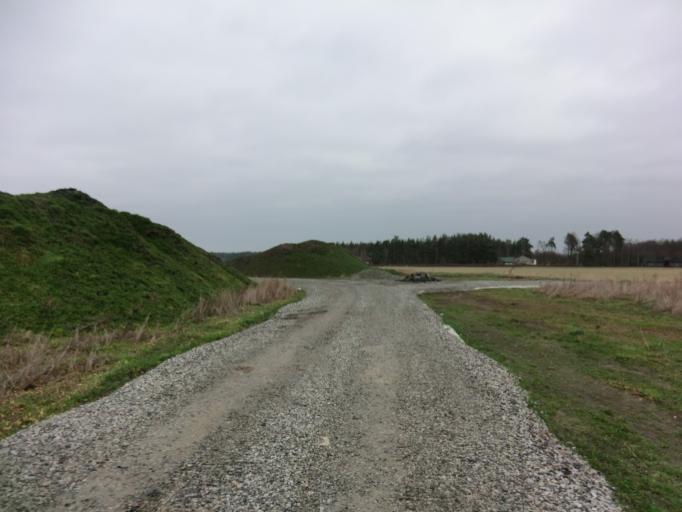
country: SE
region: Skane
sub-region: Lunds Kommun
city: Genarp
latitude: 55.7236
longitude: 13.3599
